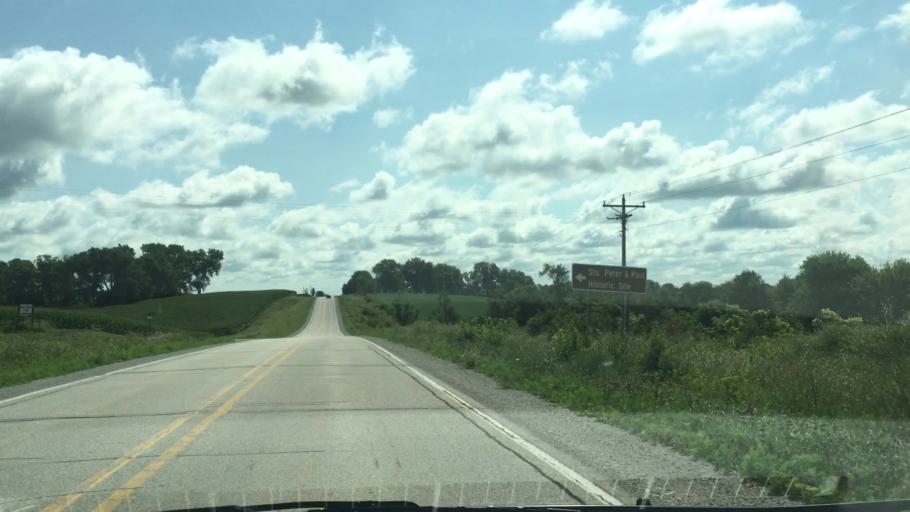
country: US
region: Iowa
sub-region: Johnson County
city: Solon
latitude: 41.8310
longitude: -91.4648
